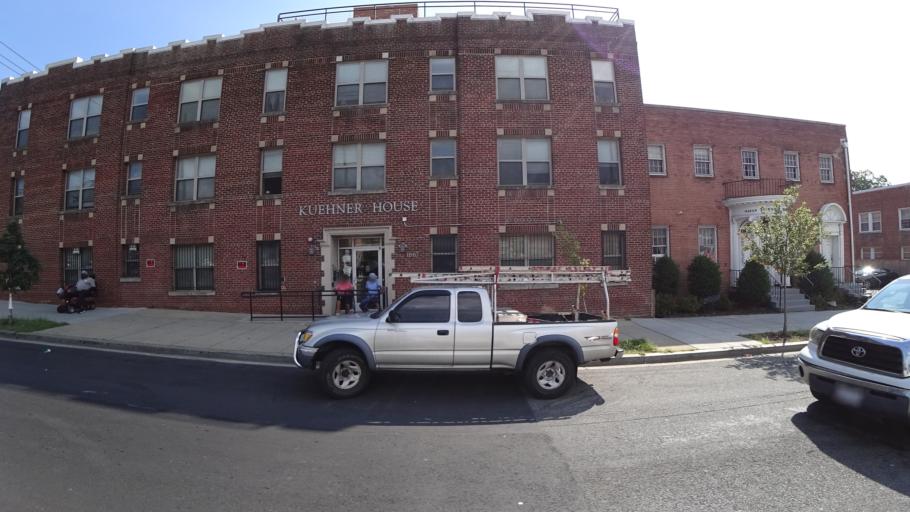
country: US
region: Maryland
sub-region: Prince George's County
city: Hillcrest Heights
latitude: 38.8658
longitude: -76.9798
